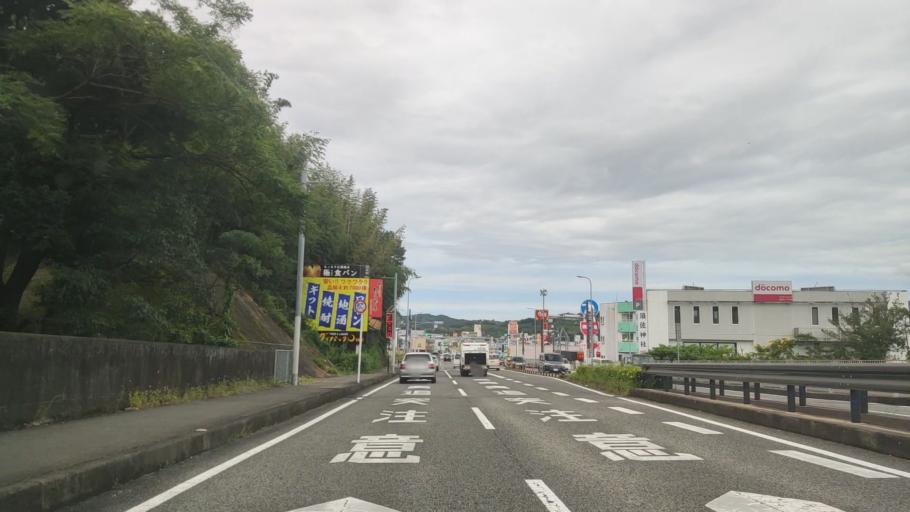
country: JP
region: Wakayama
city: Tanabe
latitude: 33.7372
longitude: 135.3971
